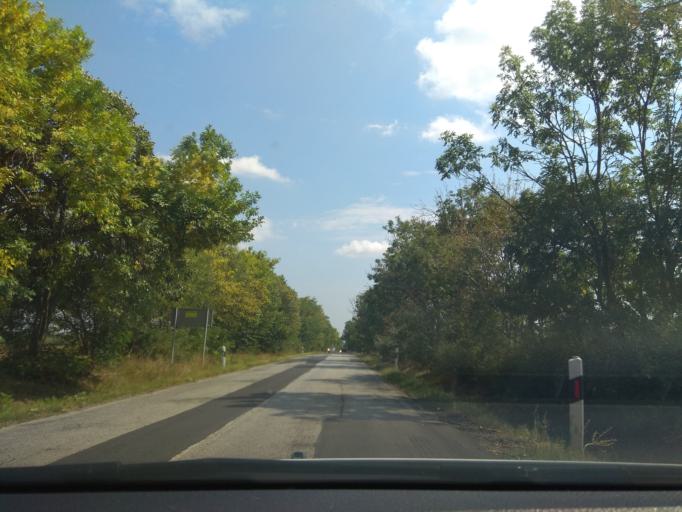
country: HU
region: Heves
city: Szihalom
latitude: 47.8211
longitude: 20.4944
